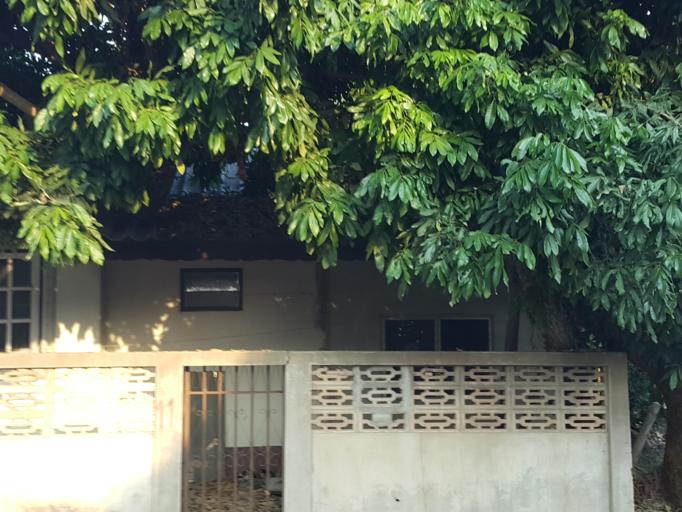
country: TH
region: Chiang Mai
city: San Sai
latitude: 18.9040
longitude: 98.9430
